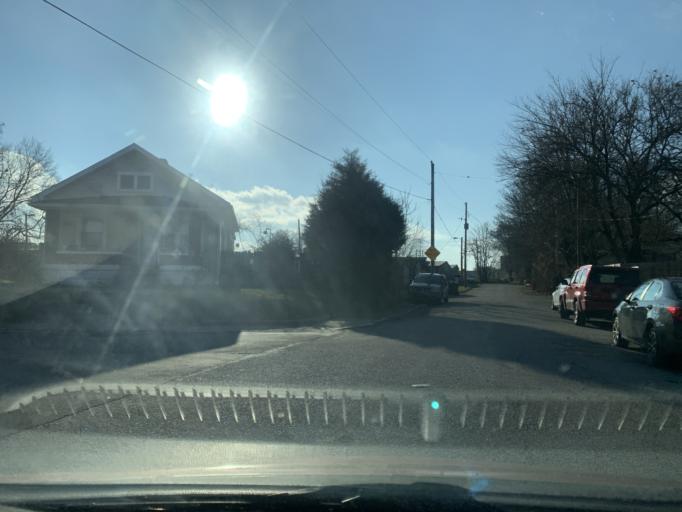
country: US
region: Kentucky
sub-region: Jefferson County
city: Audubon Park
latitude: 38.2319
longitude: -85.7382
